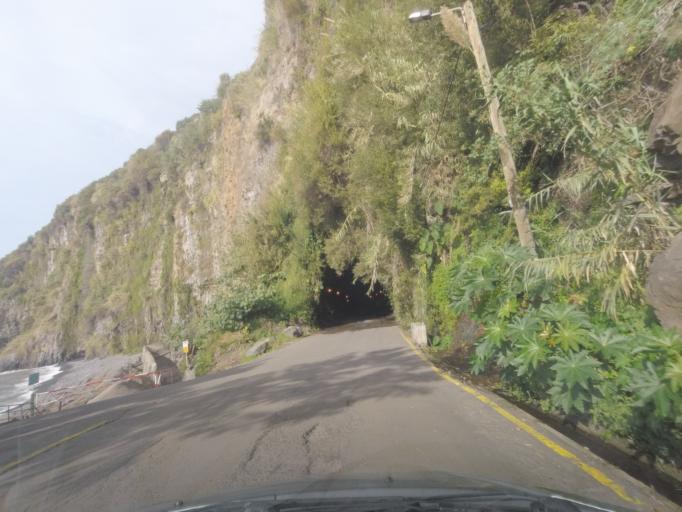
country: PT
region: Madeira
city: Ponta do Sol
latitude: 32.6907
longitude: -17.1198
